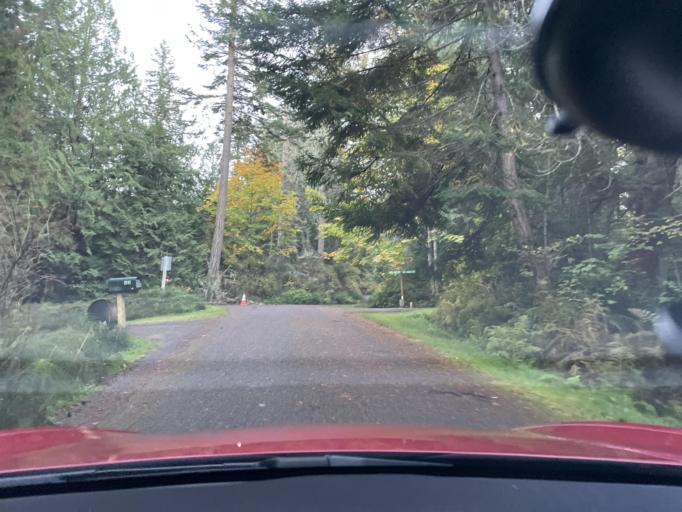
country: US
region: Washington
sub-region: San Juan County
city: Friday Harbor
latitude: 48.6186
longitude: -123.1411
